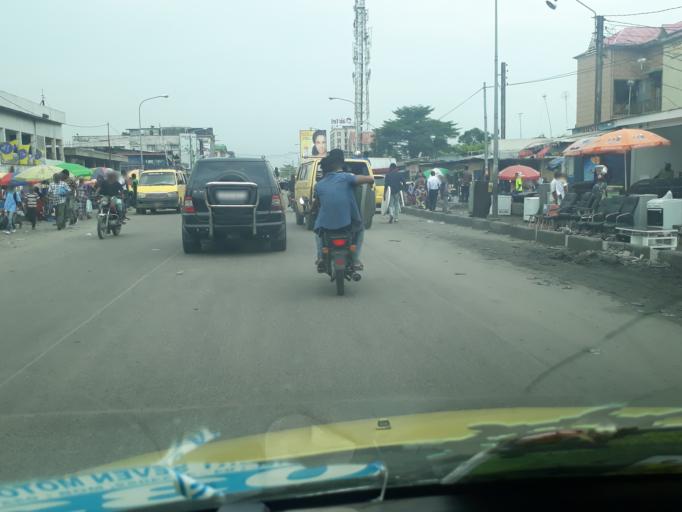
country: CD
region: Kinshasa
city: Kinshasa
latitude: -4.3449
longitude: 15.3124
